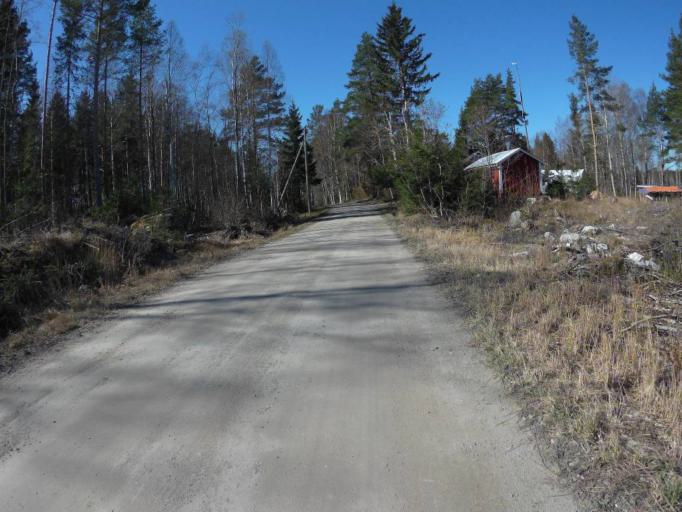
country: SE
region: Gaevleborg
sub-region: Gavle Kommun
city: Gavle
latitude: 60.7512
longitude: 17.2499
